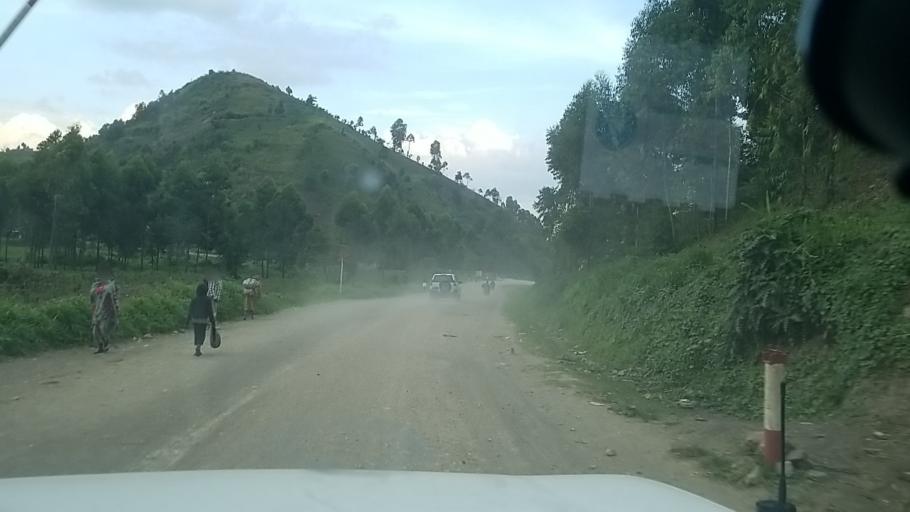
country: CD
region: Nord Kivu
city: Sake
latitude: -1.5702
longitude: 29.0457
